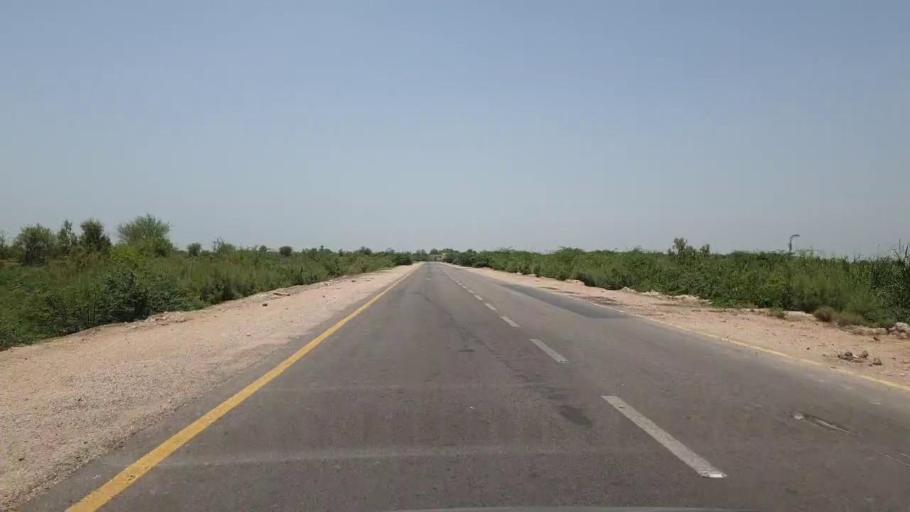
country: PK
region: Sindh
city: Sakrand
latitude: 26.1135
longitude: 68.3878
